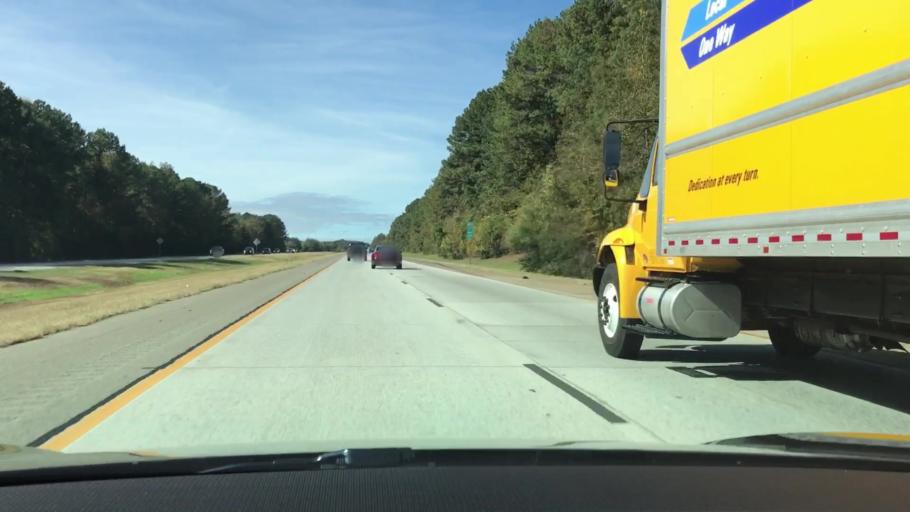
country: US
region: Georgia
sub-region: Morgan County
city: Madison
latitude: 33.5543
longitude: -83.3948
